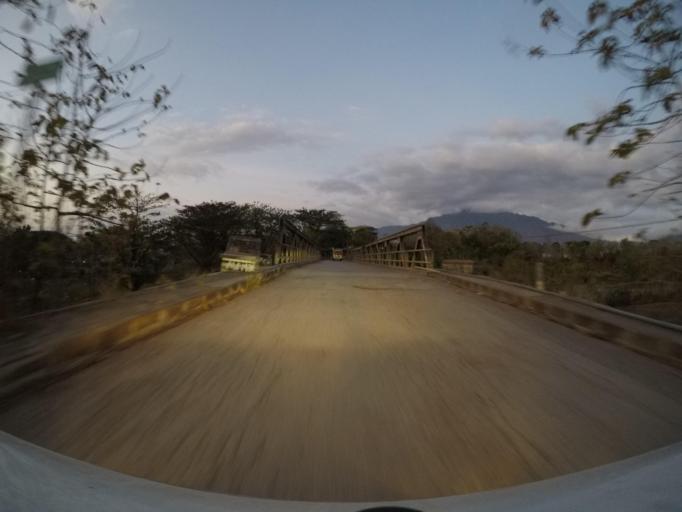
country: TL
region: Bobonaro
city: Maliana
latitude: -8.9929
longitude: 125.1937
